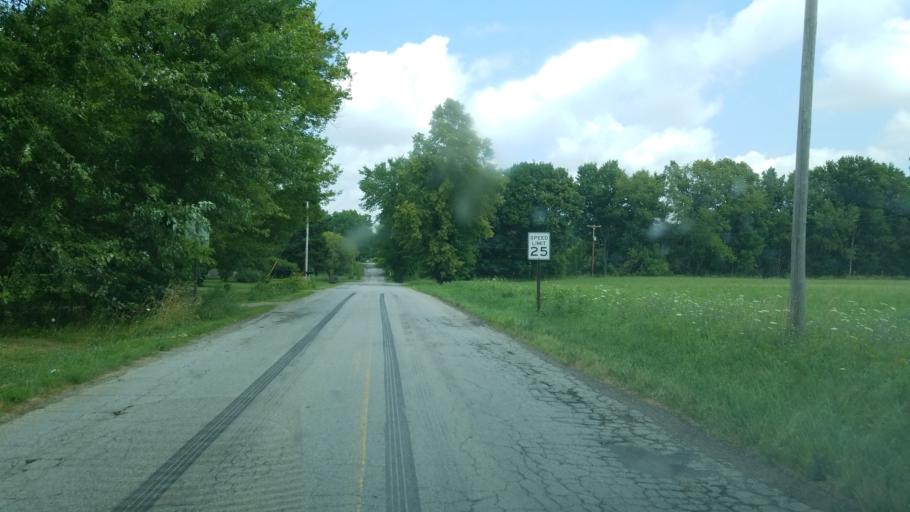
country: US
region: Michigan
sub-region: Kent County
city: Cedar Springs
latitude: 43.2883
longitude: -85.5115
